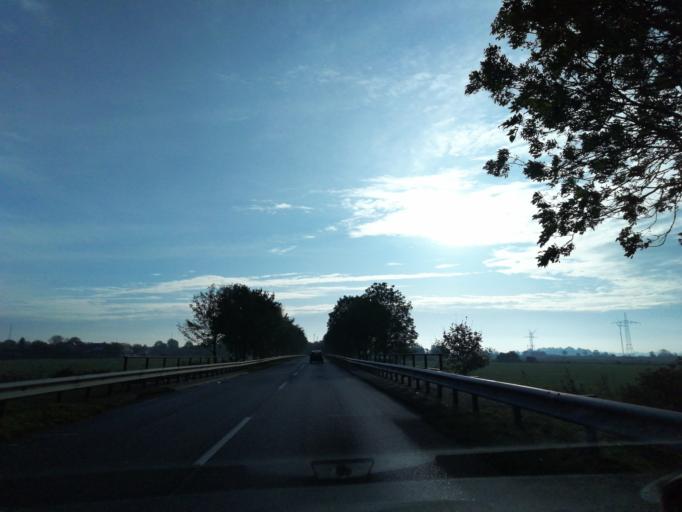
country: DE
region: Lower Saxony
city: Sillenstede
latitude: 53.6233
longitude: 8.0186
